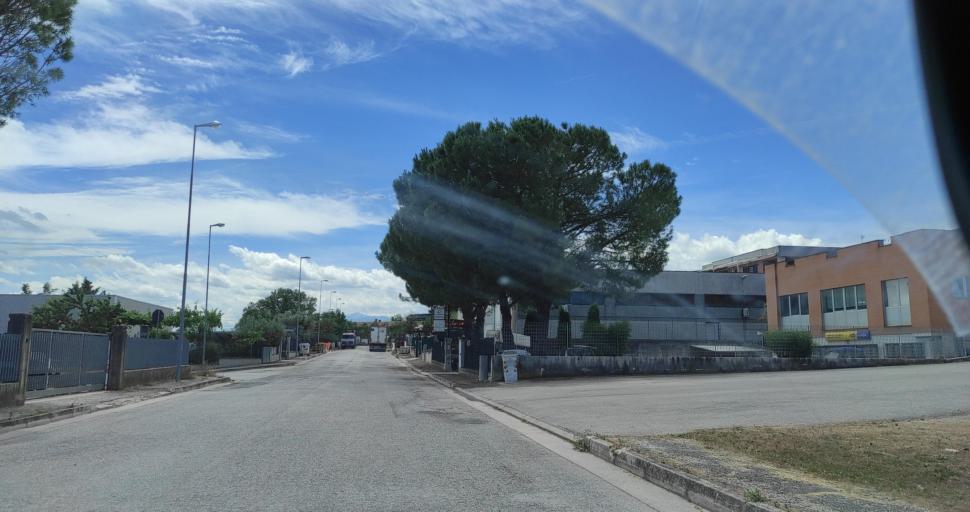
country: IT
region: The Marches
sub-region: Provincia di Macerata
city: Urbisaglia
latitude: 43.2100
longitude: 13.3933
